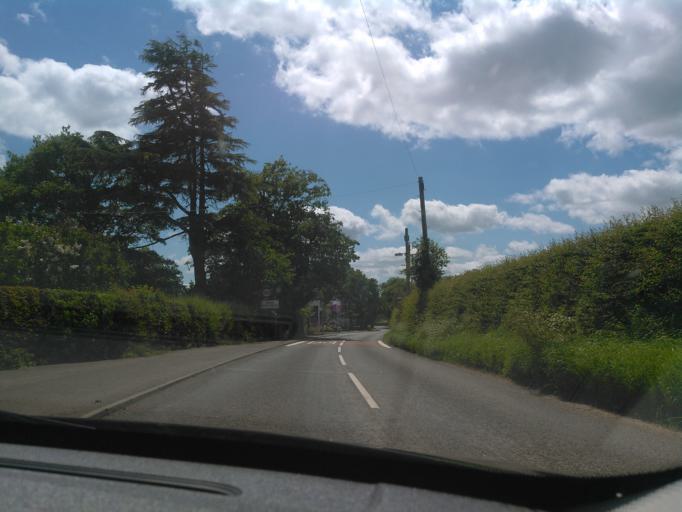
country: GB
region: England
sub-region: Shropshire
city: Wem
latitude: 52.8643
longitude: -2.7197
